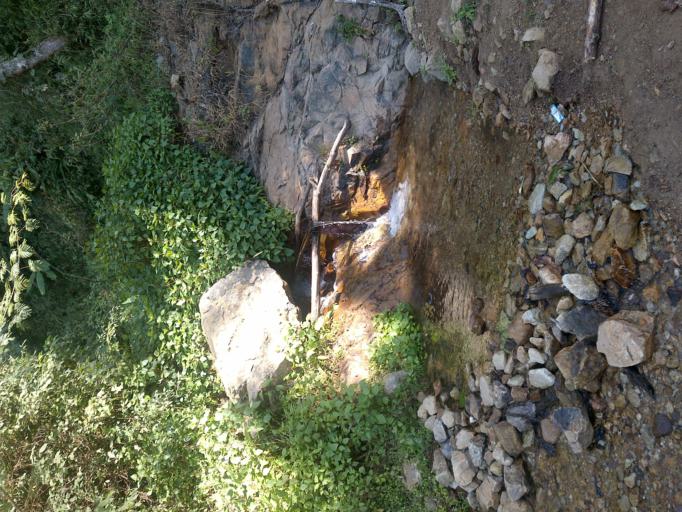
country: LA
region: Houaphan
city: Xam Nua
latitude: 20.4122
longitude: 103.8541
